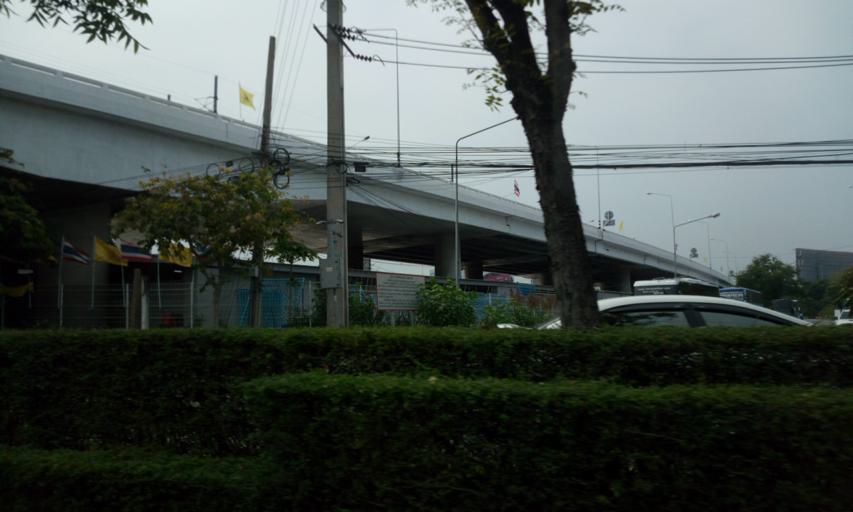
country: TH
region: Bangkok
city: Lat Krabang
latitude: 13.7216
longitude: 100.7599
